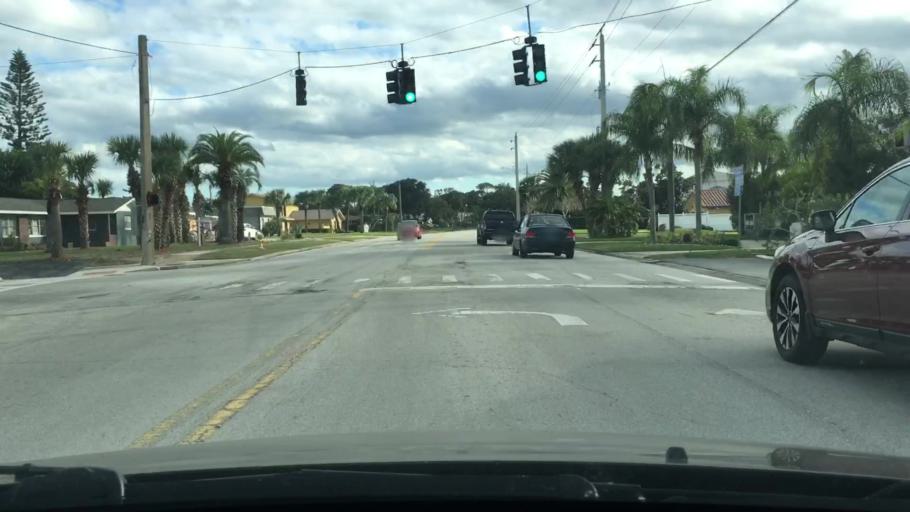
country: US
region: Florida
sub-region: Volusia County
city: Holly Hill
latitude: 29.2625
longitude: -81.0340
